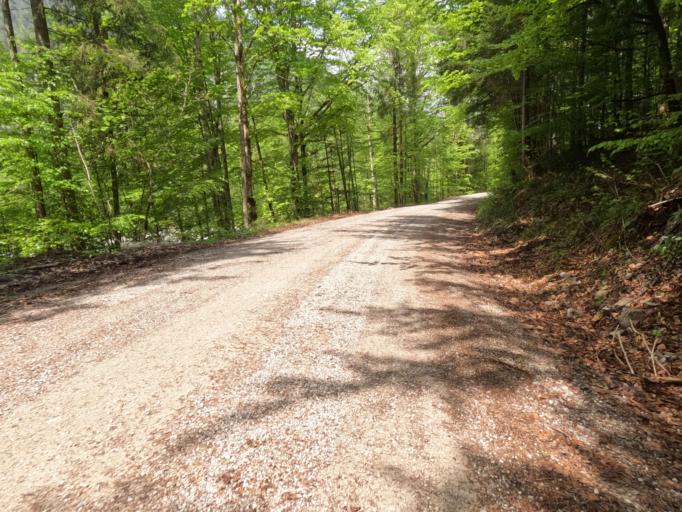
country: DE
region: Bavaria
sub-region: Upper Bavaria
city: Ruhpolding
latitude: 47.7170
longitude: 12.6603
